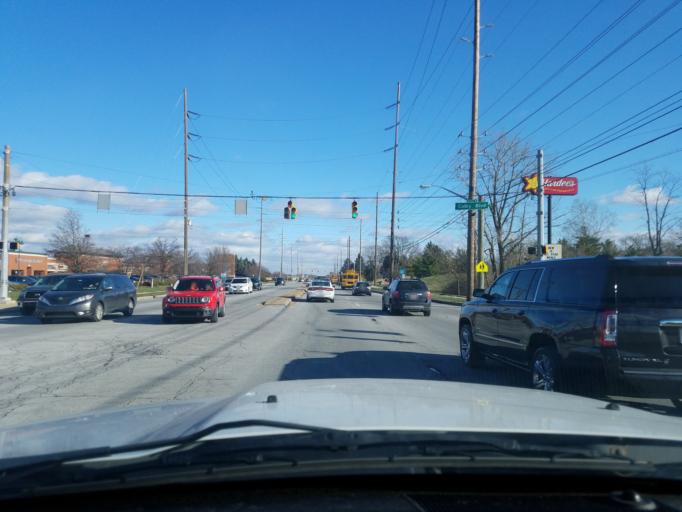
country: US
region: Indiana
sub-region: Marion County
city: Meridian Hills
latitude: 39.9118
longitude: -86.2134
